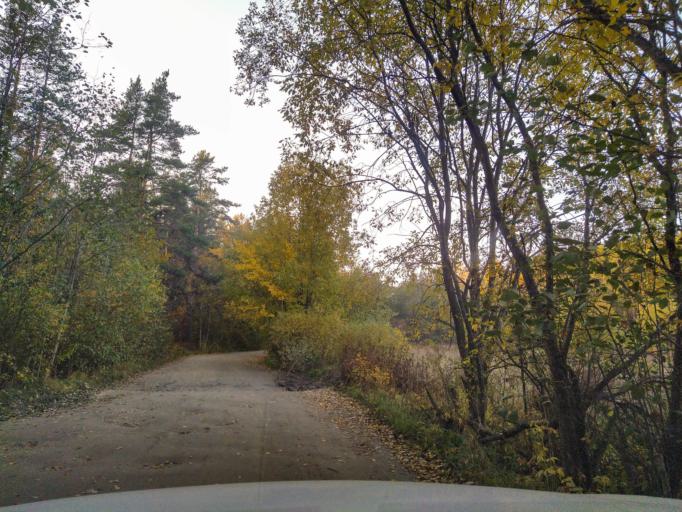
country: RU
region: Leningrad
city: Kuznechnoye
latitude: 61.2978
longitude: 30.0594
